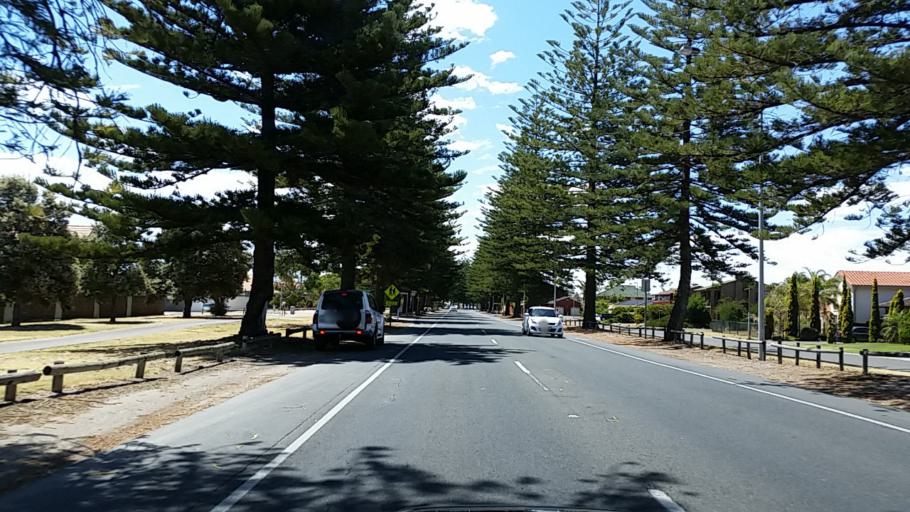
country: AU
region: South Australia
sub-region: Port Adelaide Enfield
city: Birkenhead
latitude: -34.7911
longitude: 138.4908
